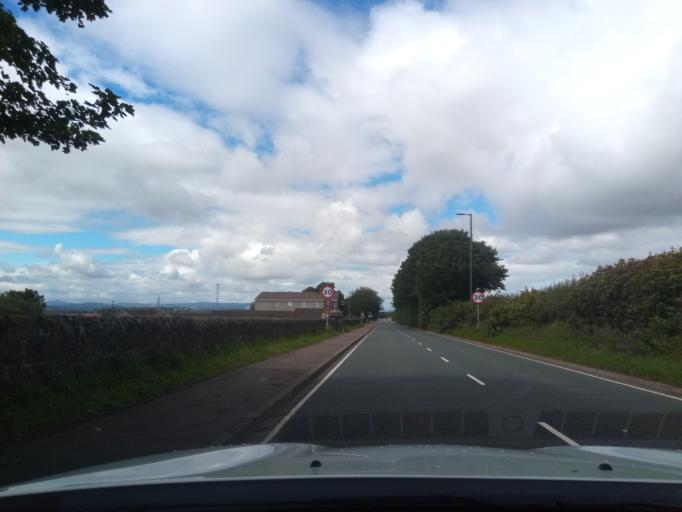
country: GB
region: Scotland
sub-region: Fife
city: Kincardine
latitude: 56.0668
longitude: -3.7060
